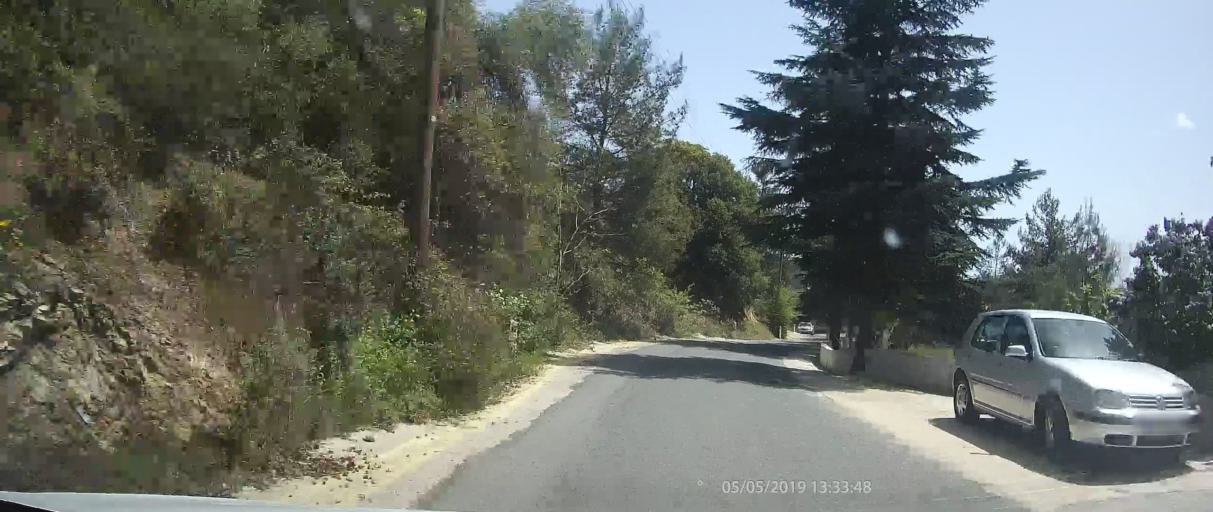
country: CY
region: Limassol
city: Pelendri
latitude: 34.8847
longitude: 32.8582
